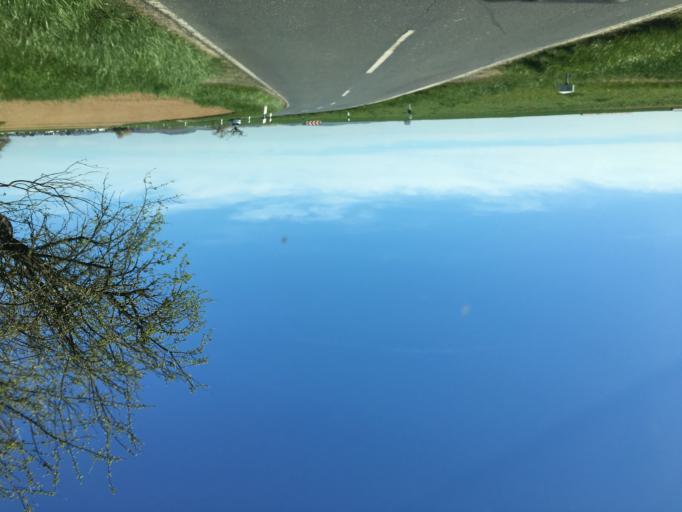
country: DE
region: Hesse
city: Dieburg
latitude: 49.8699
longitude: 8.8736
